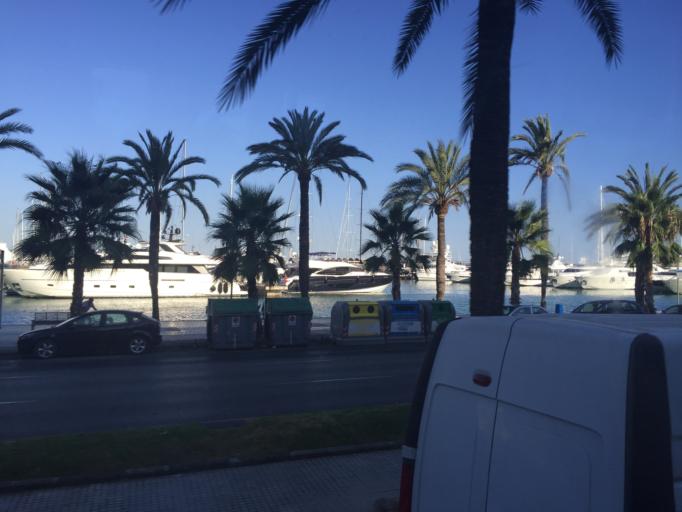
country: ES
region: Balearic Islands
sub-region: Illes Balears
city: Palma
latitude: 39.5657
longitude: 2.6286
